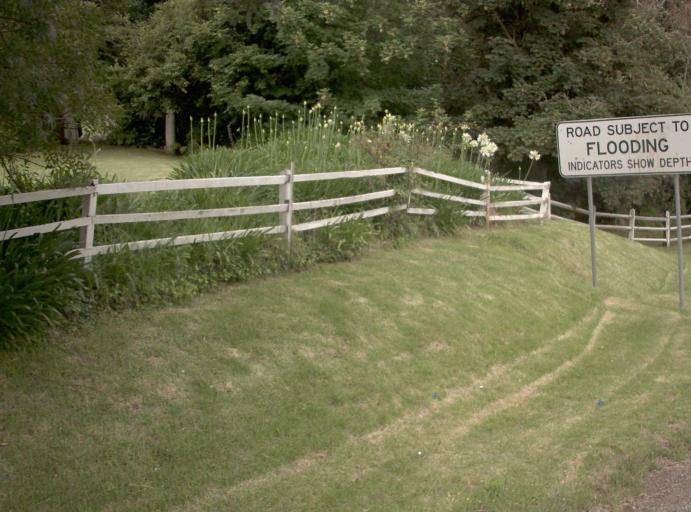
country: AU
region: Victoria
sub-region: East Gippsland
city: Bairnsdale
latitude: -37.8193
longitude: 147.6202
